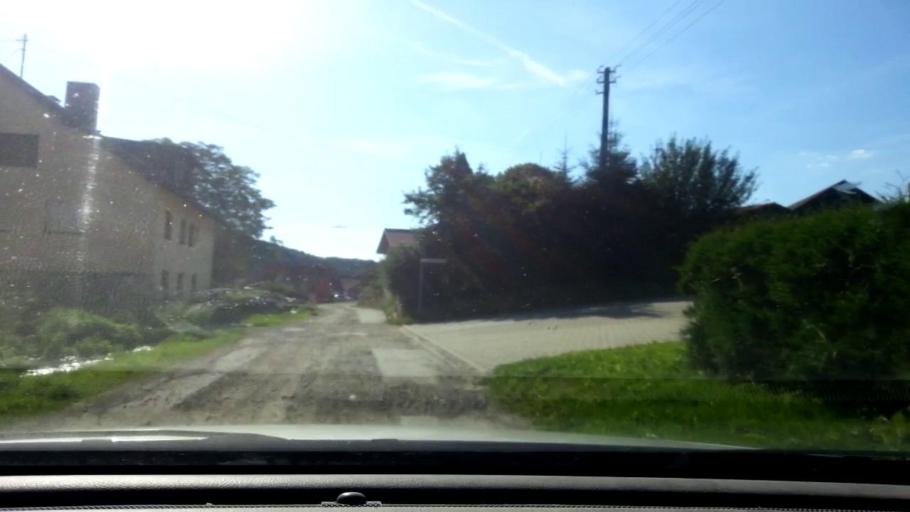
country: DE
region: Bavaria
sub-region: Upper Franconia
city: Schesslitz
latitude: 49.9961
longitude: 11.0840
